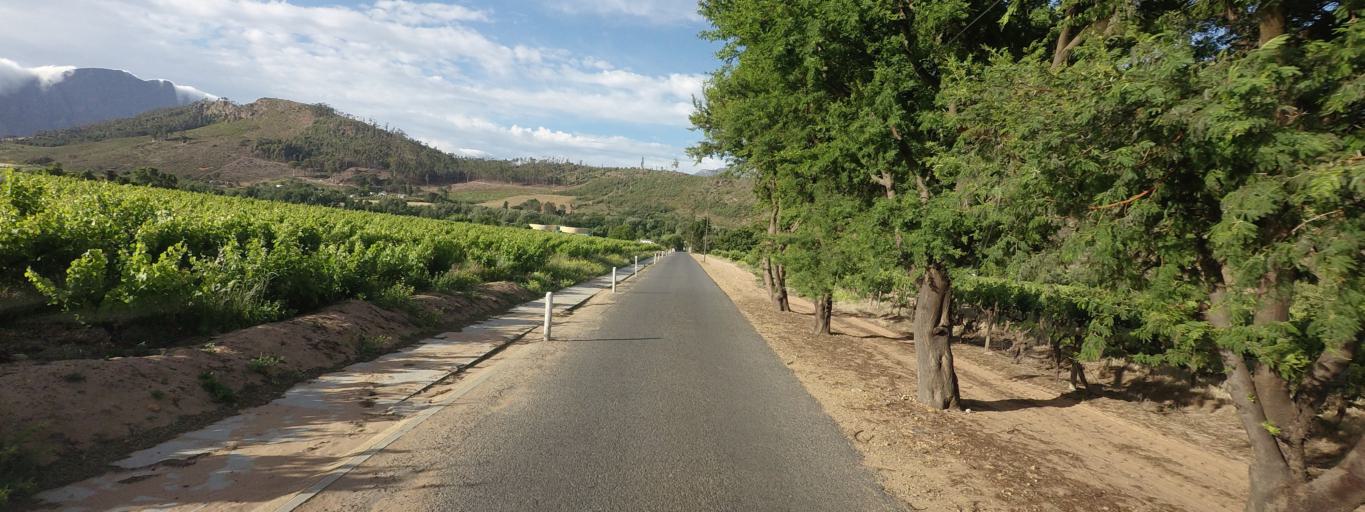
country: ZA
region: Western Cape
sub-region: Cape Winelands District Municipality
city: Paarl
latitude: -33.8954
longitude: 19.0960
